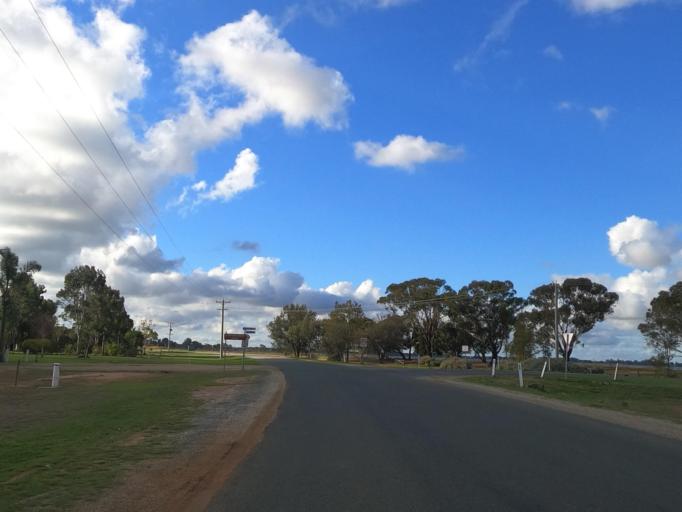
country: AU
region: Victoria
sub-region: Swan Hill
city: Swan Hill
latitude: -35.4480
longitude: 143.6266
